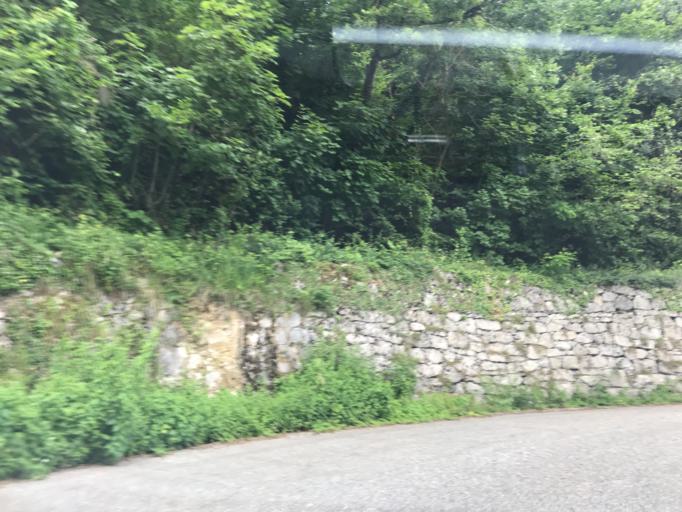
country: FR
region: Rhone-Alpes
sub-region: Departement de la Savoie
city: Mercury
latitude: 45.6793
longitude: 6.3324
